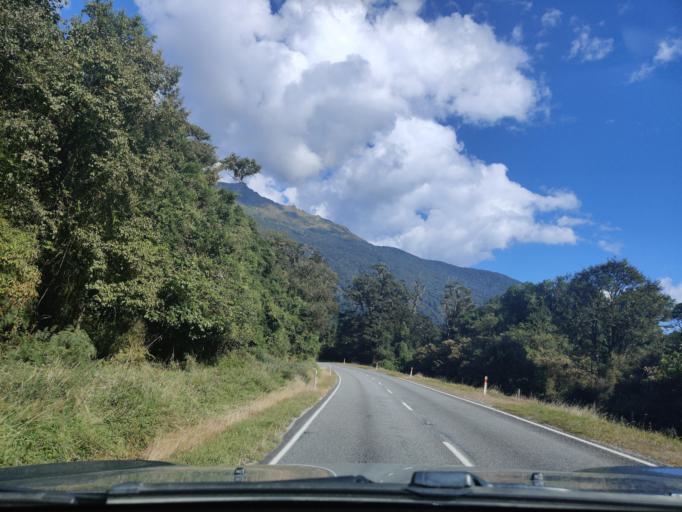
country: NZ
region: Otago
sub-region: Queenstown-Lakes District
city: Wanaka
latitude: -43.9697
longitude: 169.4003
